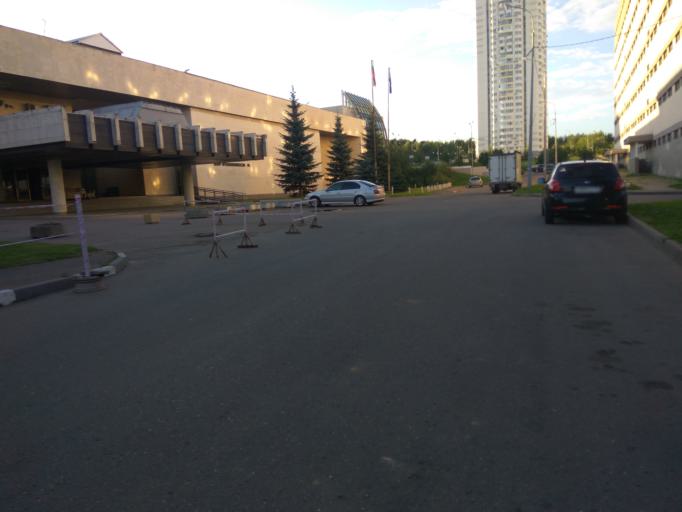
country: RU
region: Moscow
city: Chertanovo Yuzhnoye
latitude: 55.6100
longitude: 37.5776
